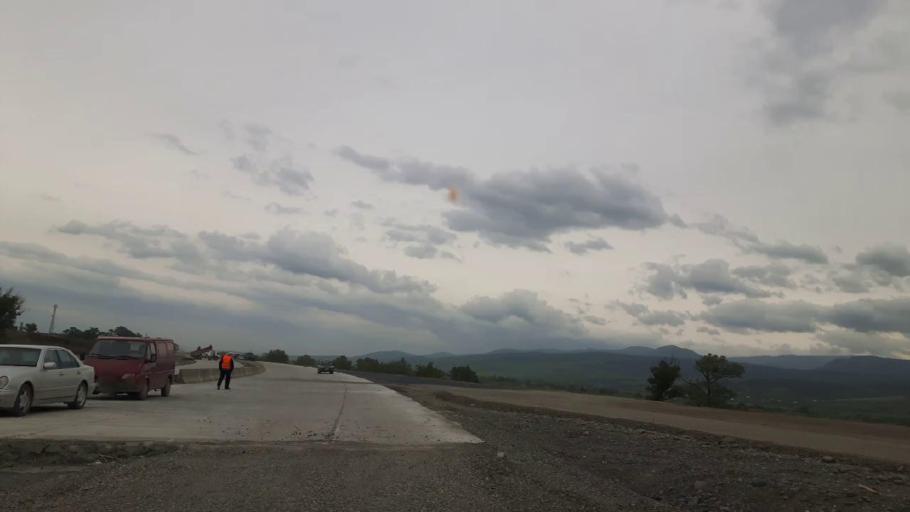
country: GE
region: Shida Kartli
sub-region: Khashuris Raioni
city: Khashuri
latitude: 42.0107
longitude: 43.7043
